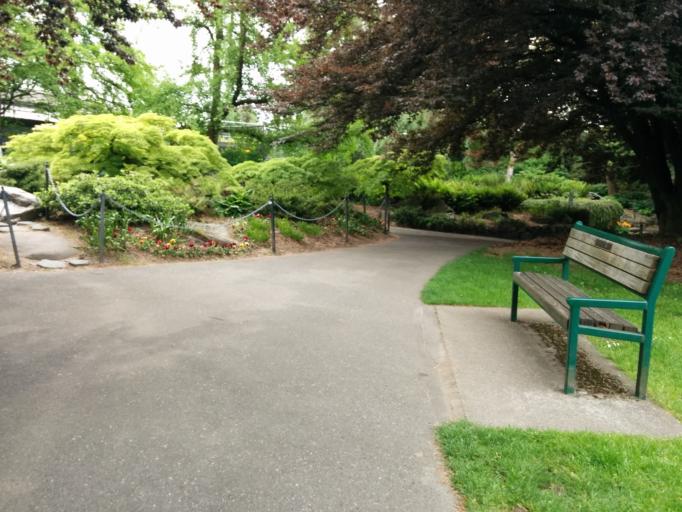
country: CA
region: British Columbia
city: Vancouver
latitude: 49.2420
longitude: -123.1146
